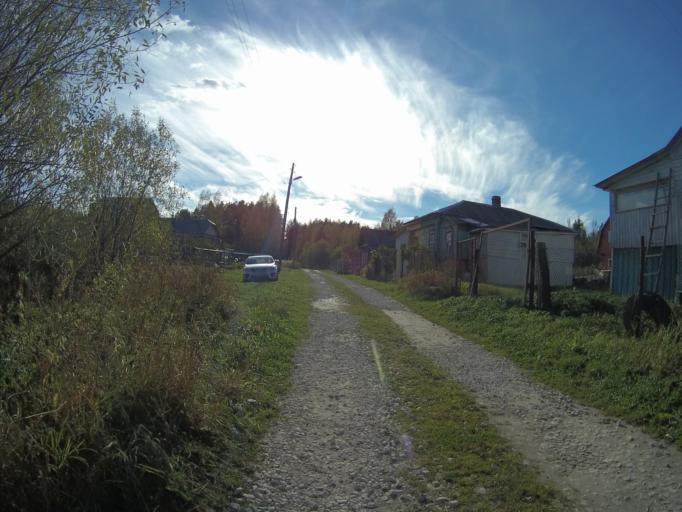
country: RU
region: Vladimir
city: Golovino
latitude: 55.9902
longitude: 40.5227
